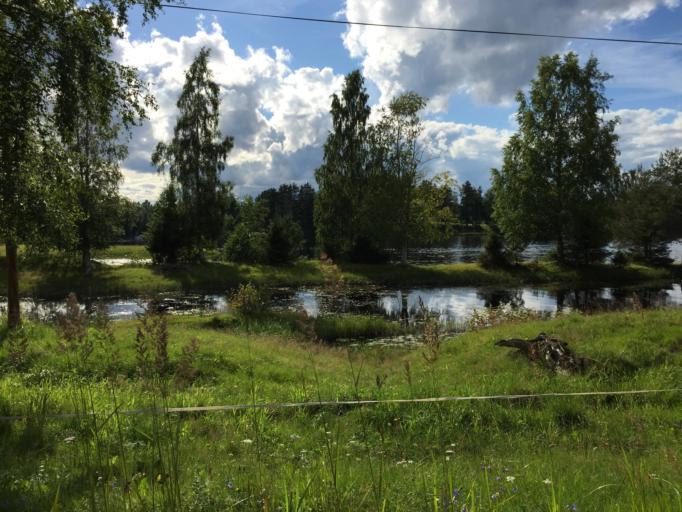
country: SE
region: Gaevleborg
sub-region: Ljusdals Kommun
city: Jaervsoe
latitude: 61.7608
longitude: 16.1704
